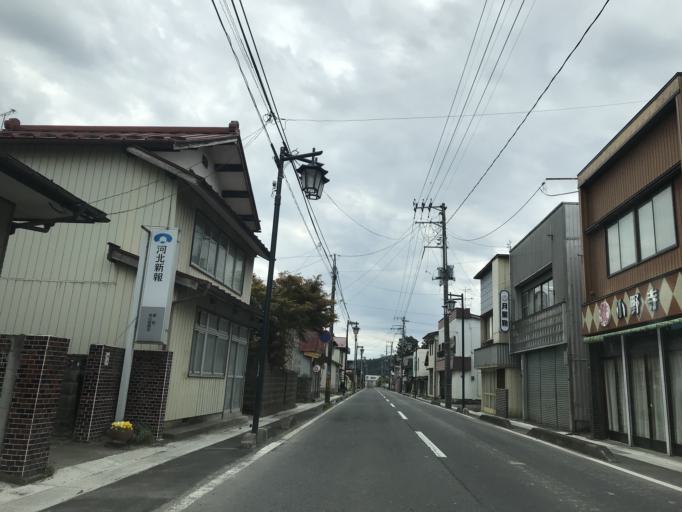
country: JP
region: Iwate
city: Ichinoseki
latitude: 38.7686
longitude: 141.3287
